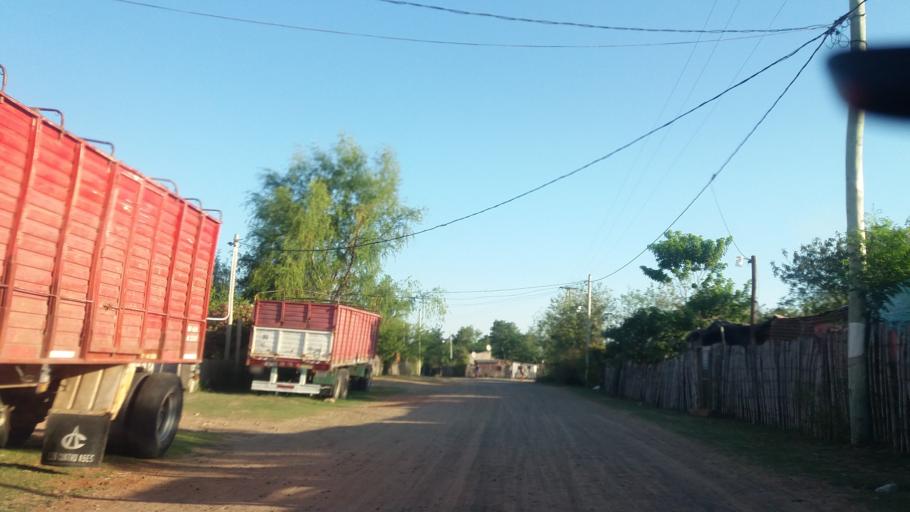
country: AR
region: Corrientes
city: Corrientes
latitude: -27.5182
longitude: -58.8297
